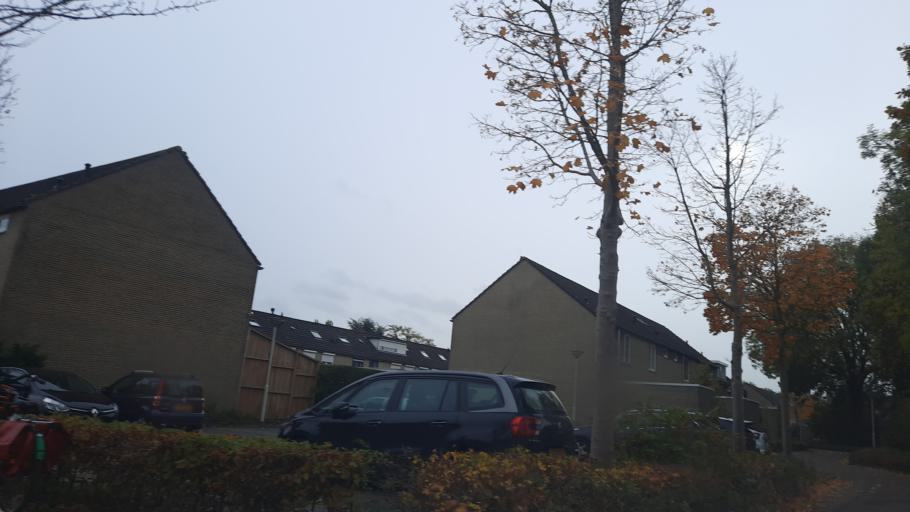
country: NL
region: South Holland
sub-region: Gemeente Gorinchem
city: Gorinchem
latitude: 51.8426
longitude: 4.9599
